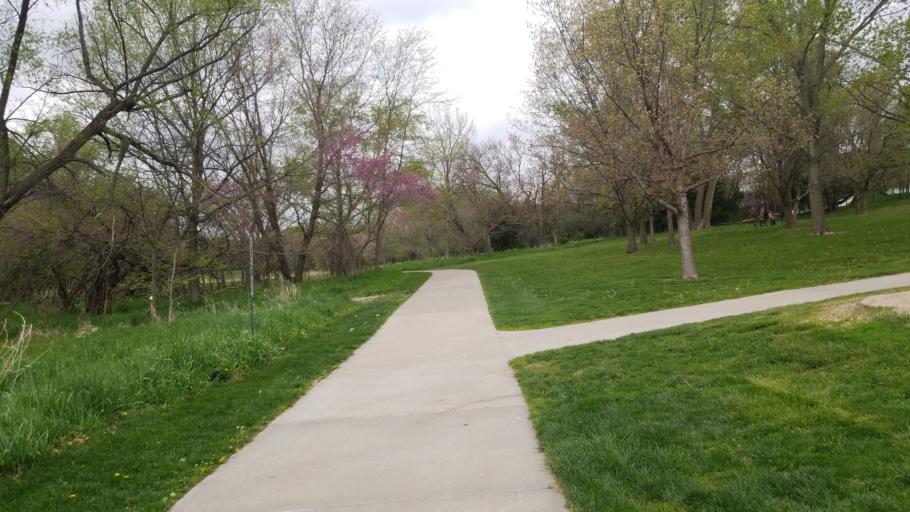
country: US
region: Nebraska
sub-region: Sarpy County
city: Chalco
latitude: 41.1719
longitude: -96.1616
